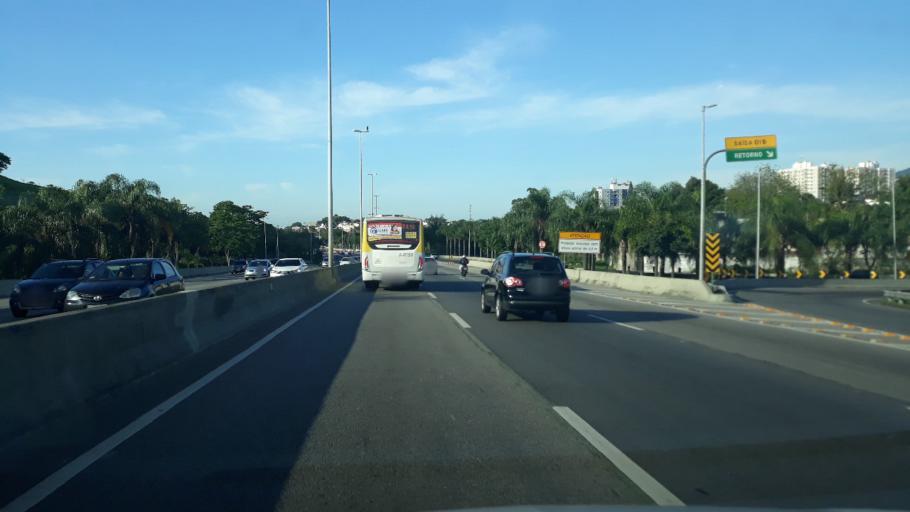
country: BR
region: Rio de Janeiro
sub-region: Sao Joao De Meriti
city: Sao Joao de Meriti
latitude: -22.9390
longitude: -43.3500
